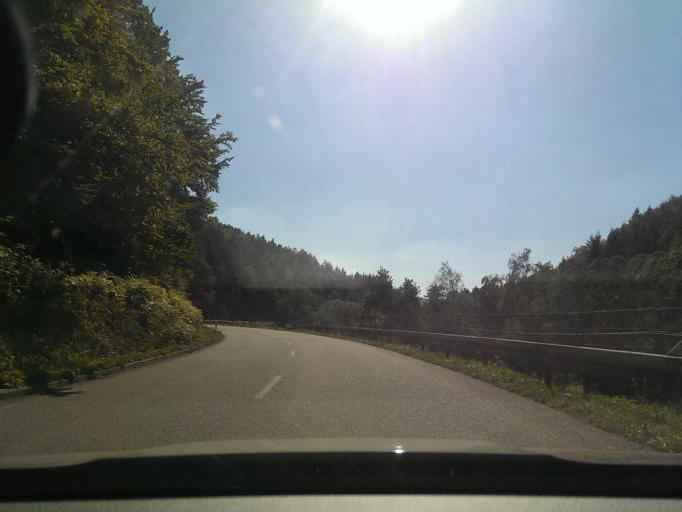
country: DE
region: Baden-Wuerttemberg
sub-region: Karlsruhe Region
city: Bad Herrenalb
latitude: 48.8435
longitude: 8.4392
